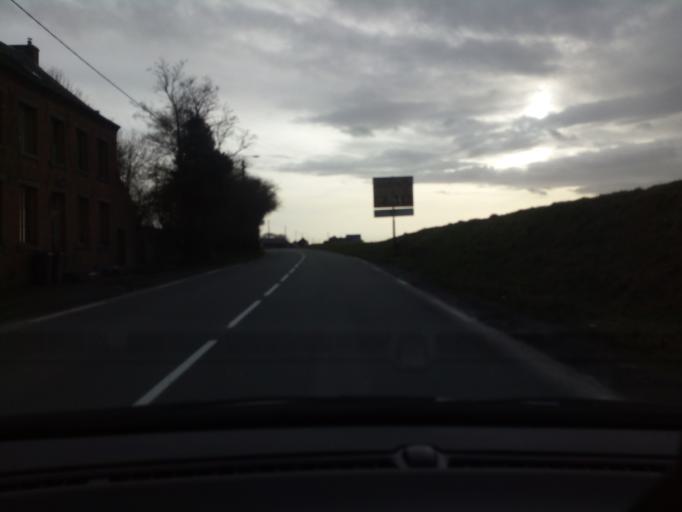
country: FR
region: Nord-Pas-de-Calais
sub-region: Departement du Nord
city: La Longueville
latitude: 50.3308
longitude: 3.8692
